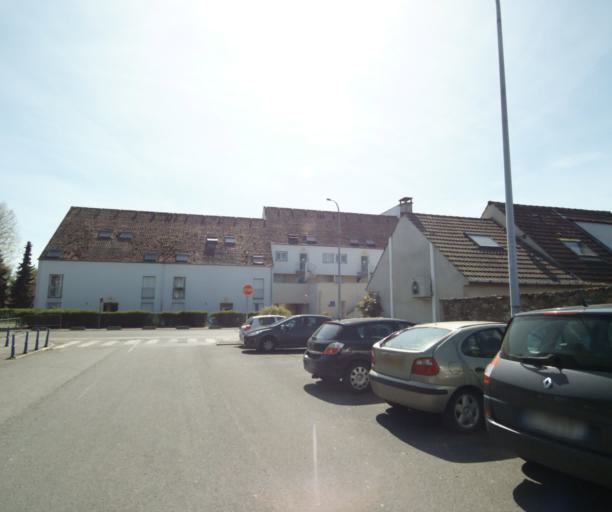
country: FR
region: Ile-de-France
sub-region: Departement de Seine-et-Marne
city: Nangis
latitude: 48.5552
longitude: 3.0116
